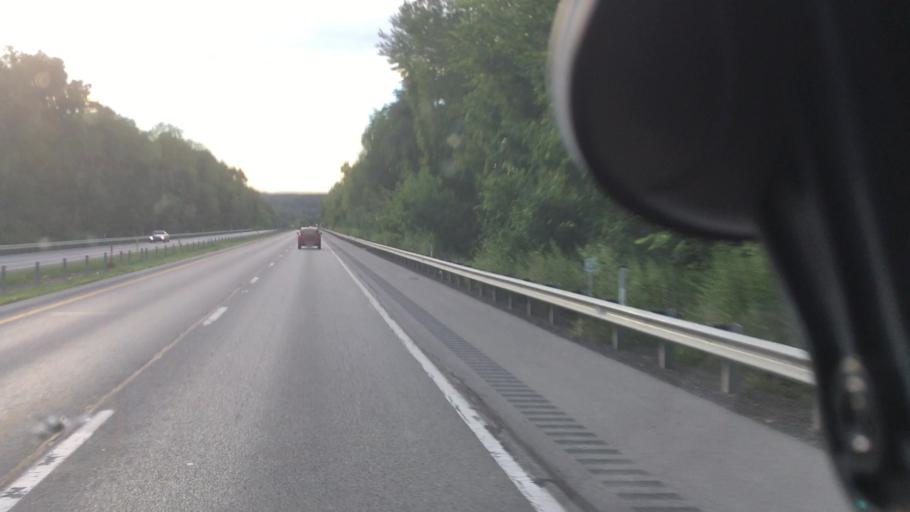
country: US
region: Pennsylvania
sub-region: Beaver County
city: Big Beaver
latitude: 40.7878
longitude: -80.4041
